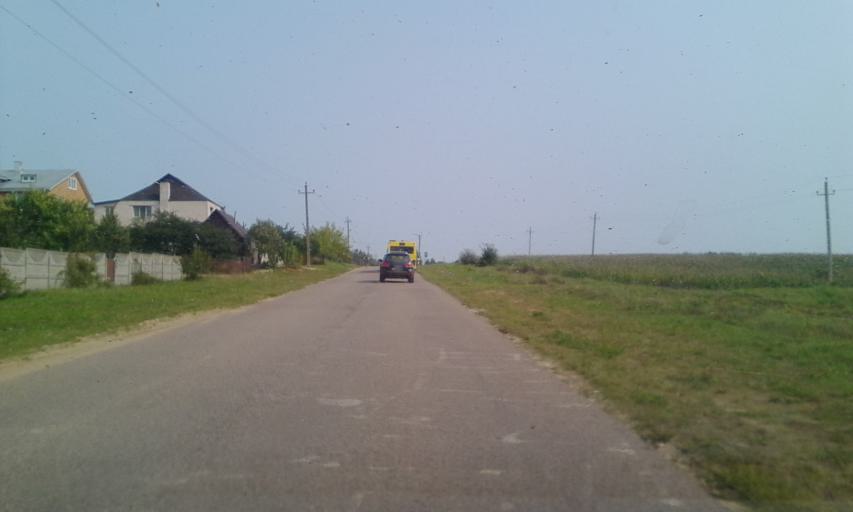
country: BY
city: Michanovichi
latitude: 53.7606
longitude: 27.6848
